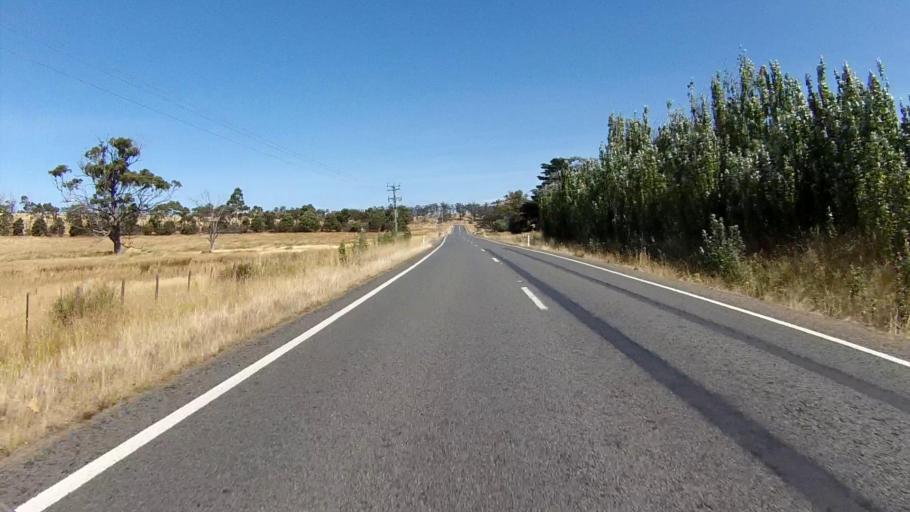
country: AU
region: Tasmania
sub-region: Sorell
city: Sorell
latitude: -42.4620
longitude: 147.9245
